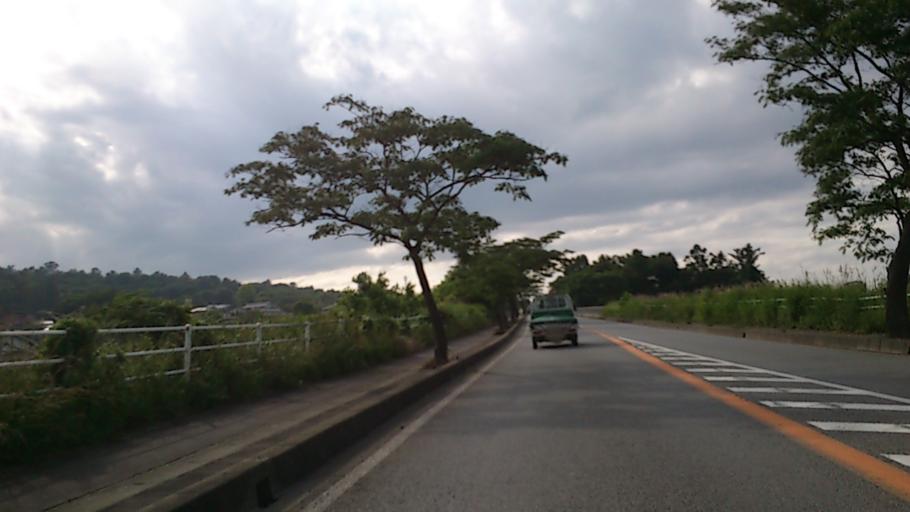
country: JP
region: Nagano
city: Saku
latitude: 36.2462
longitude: 138.4184
